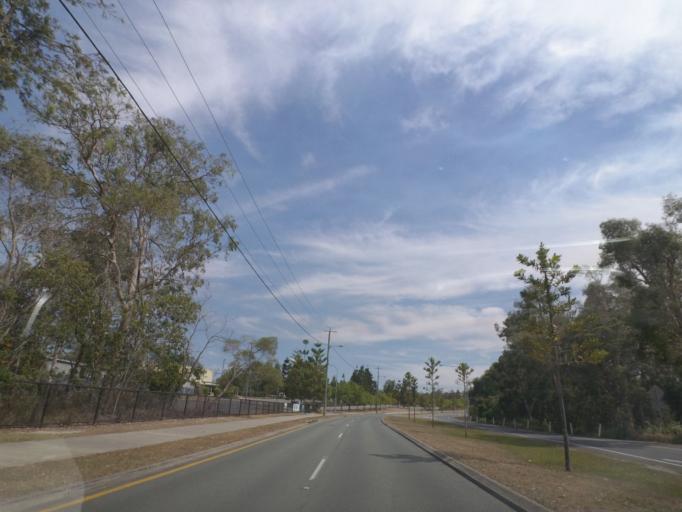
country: AU
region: Queensland
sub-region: Brisbane
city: Sunnybank Hills
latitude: -27.6360
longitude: 153.0577
